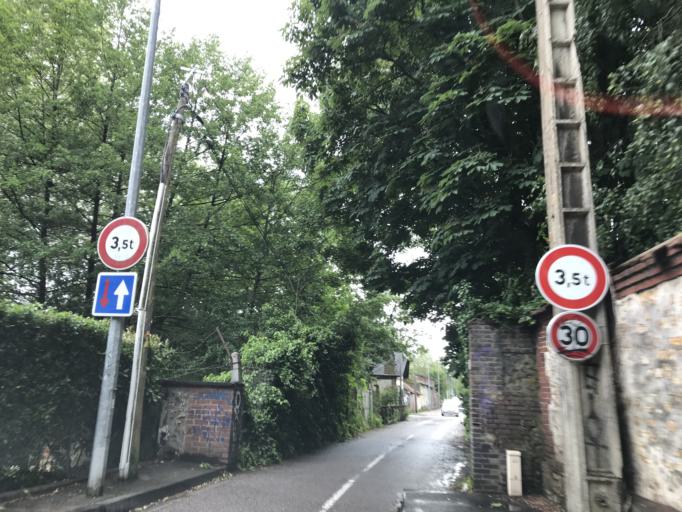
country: FR
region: Haute-Normandie
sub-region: Departement de l'Eure
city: Arnieres-sur-Iton
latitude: 49.0132
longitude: 1.1190
